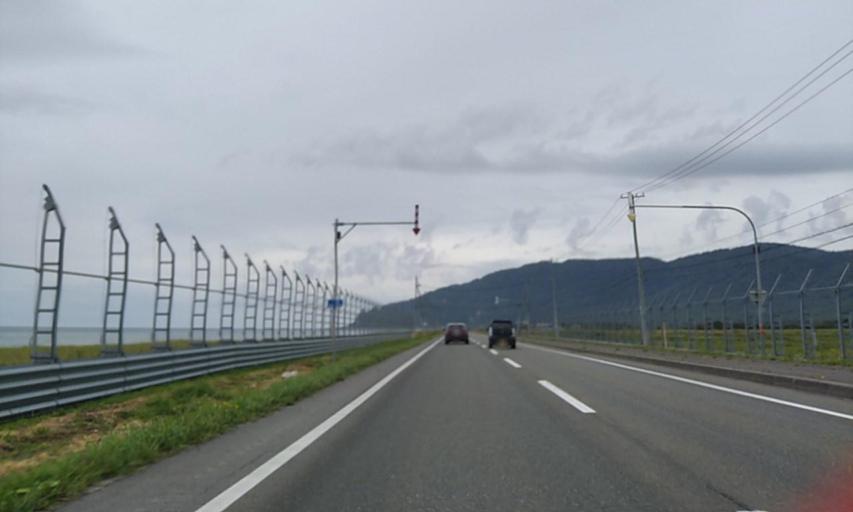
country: JP
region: Hokkaido
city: Makubetsu
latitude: 45.0836
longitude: 142.4541
